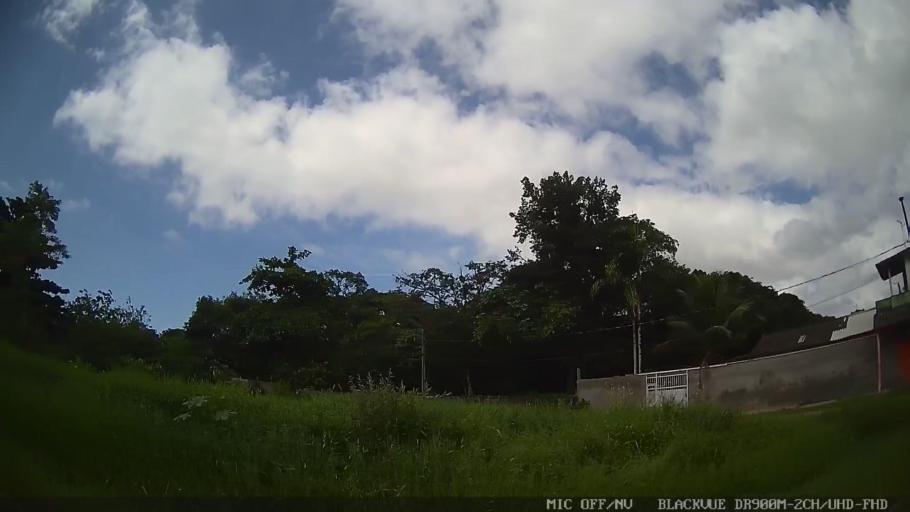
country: BR
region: Sao Paulo
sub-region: Peruibe
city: Peruibe
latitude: -24.2914
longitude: -47.0160
